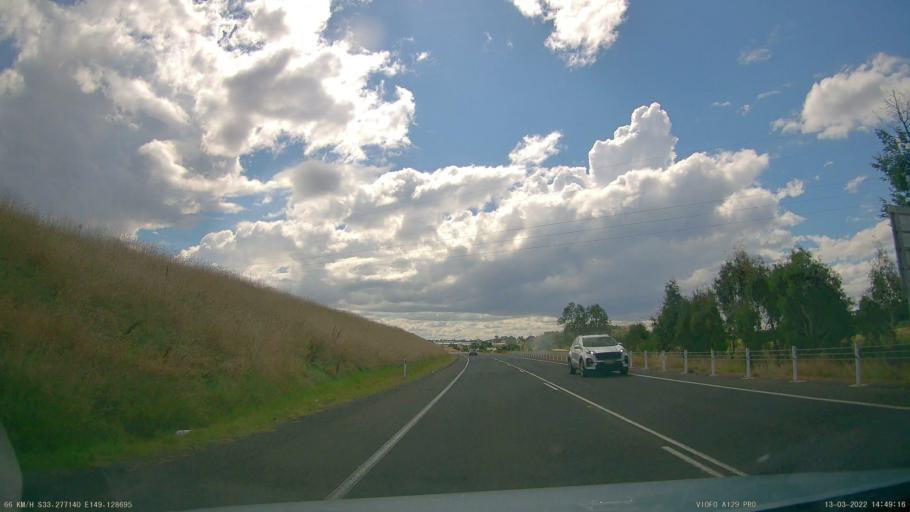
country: AU
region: New South Wales
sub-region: Orange Municipality
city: Orange
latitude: -33.2770
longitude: 149.1285
